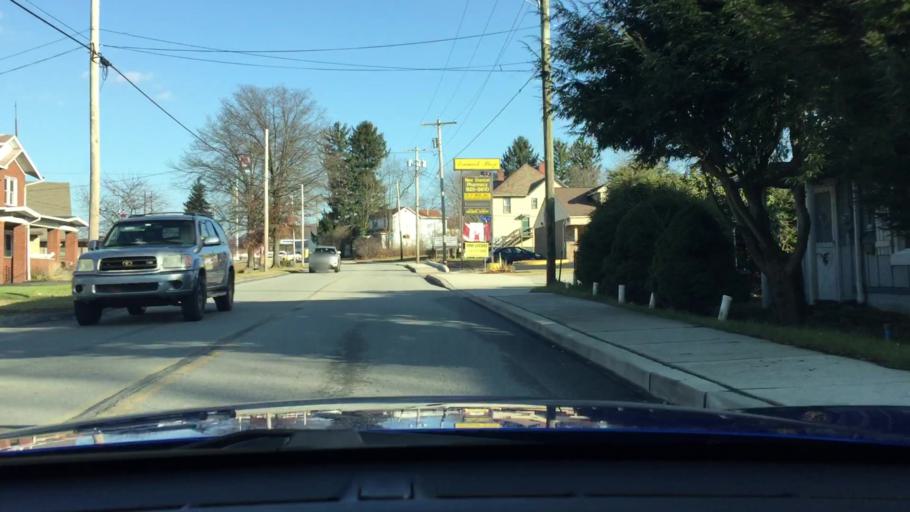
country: US
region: Pennsylvania
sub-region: Westmoreland County
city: New Stanton
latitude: 40.2160
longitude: -79.6104
